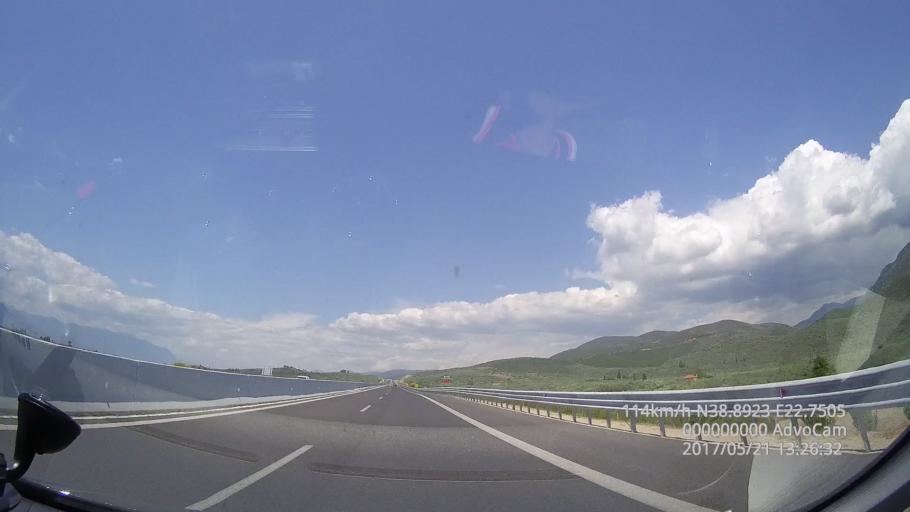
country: GR
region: Central Greece
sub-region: Nomos Fthiotidos
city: Kainouryion
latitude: 38.8924
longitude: 22.7498
